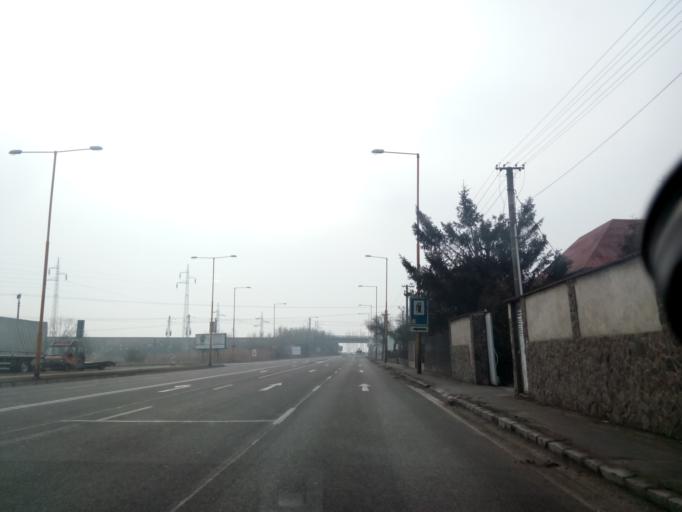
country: SK
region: Kosicky
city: Kosice
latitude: 48.6694
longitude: 21.2713
